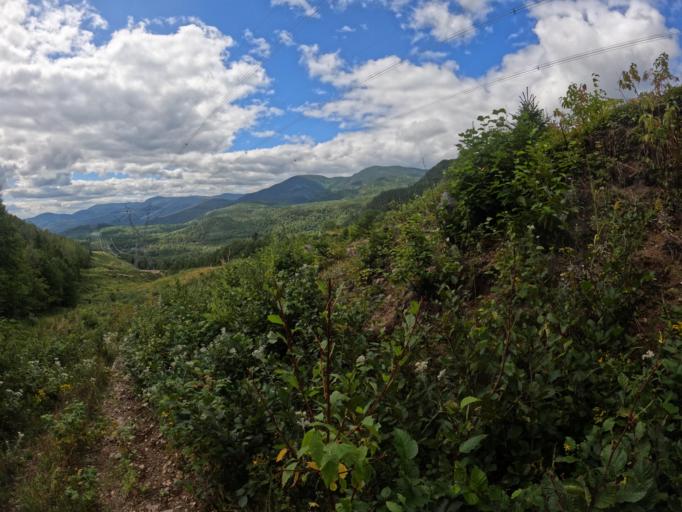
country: CA
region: Quebec
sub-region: Capitale-Nationale
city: La Malbaie
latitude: 47.8945
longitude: -70.3782
